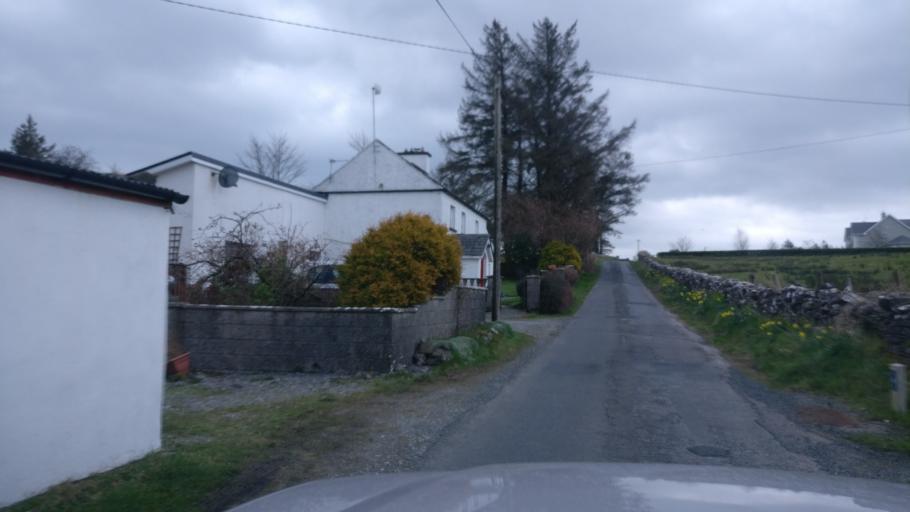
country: IE
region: Connaught
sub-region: County Galway
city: Loughrea
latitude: 53.2678
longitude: -8.4714
